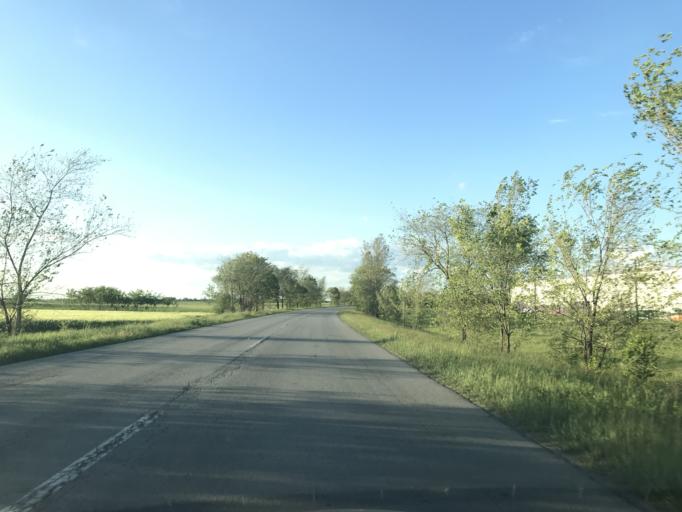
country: RS
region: Autonomna Pokrajina Vojvodina
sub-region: Srednjebanatski Okrug
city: Zrenjanin
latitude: 45.3883
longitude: 20.3523
